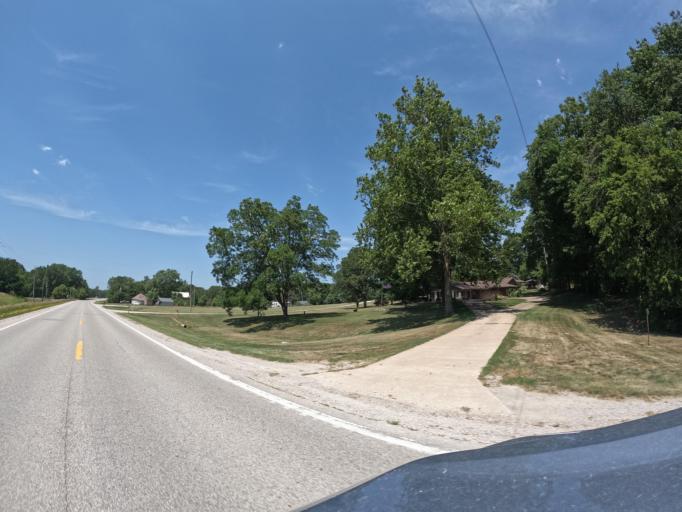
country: US
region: Iowa
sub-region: Henry County
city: Mount Pleasant
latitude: 40.9373
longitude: -91.6103
